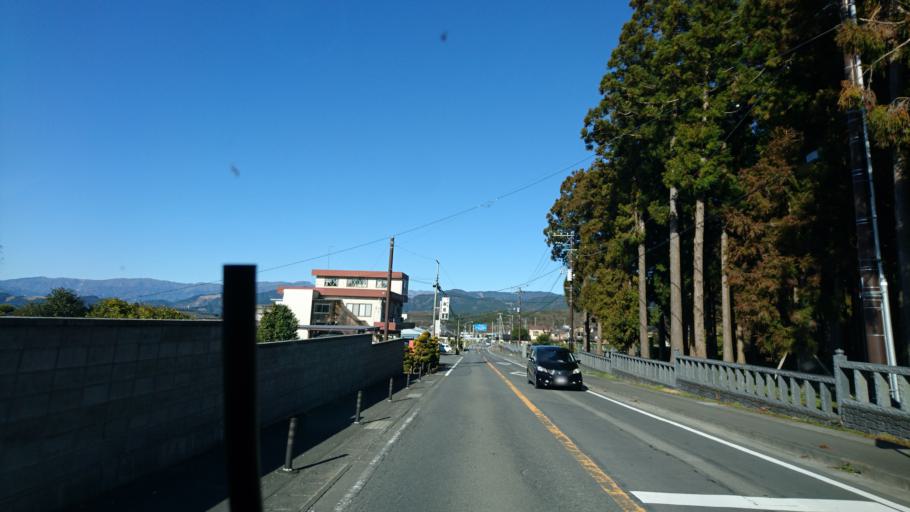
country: JP
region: Shizuoka
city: Fujinomiya
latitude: 35.2752
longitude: 138.6081
